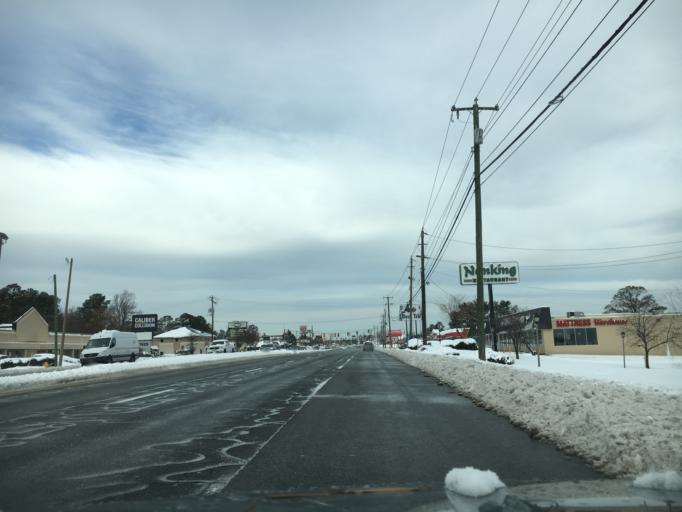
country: US
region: Virginia
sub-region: Henrico County
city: Laurel
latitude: 37.6155
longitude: -77.5219
